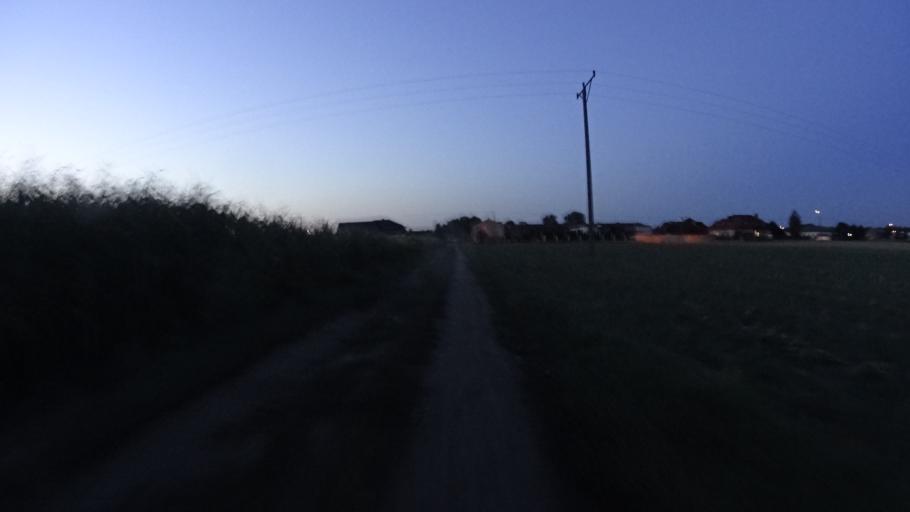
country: PL
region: Masovian Voivodeship
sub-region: Powiat warszawski zachodni
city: Ozarow Mazowiecki
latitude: 52.2282
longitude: 20.7905
